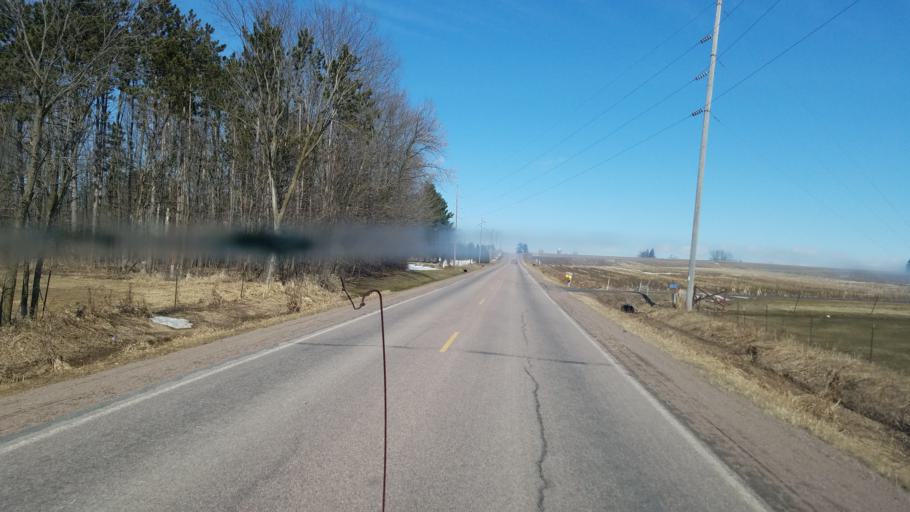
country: US
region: Wisconsin
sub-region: Clark County
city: Loyal
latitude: 44.5748
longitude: -90.3958
